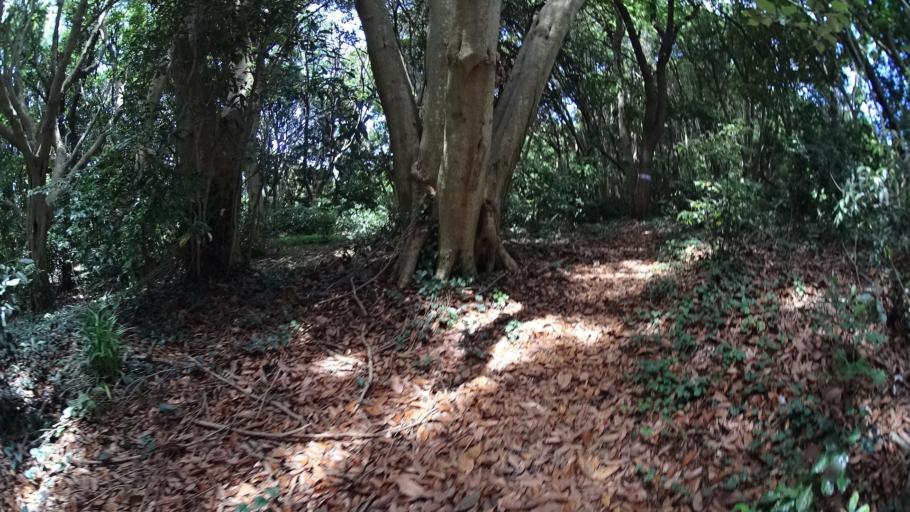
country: JP
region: Kanagawa
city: Yokosuka
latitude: 35.2091
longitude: 139.6701
